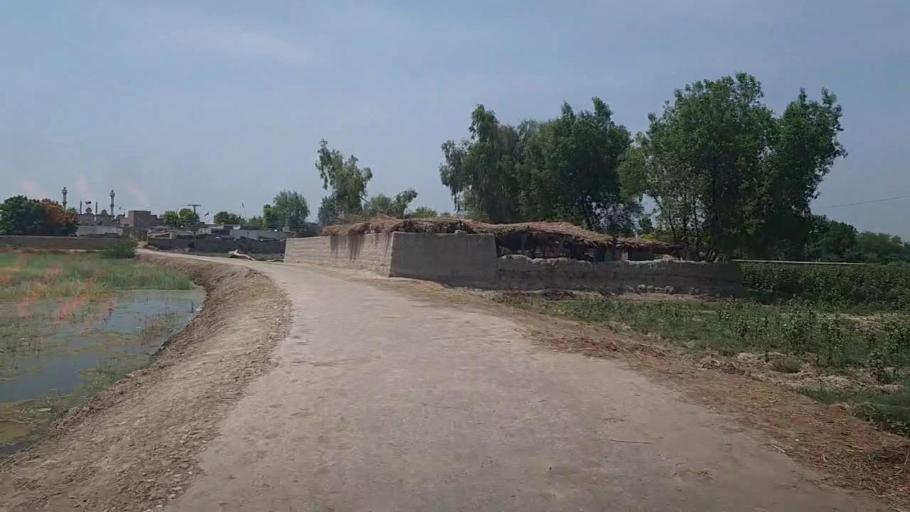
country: PK
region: Sindh
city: Ubauro
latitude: 28.1923
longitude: 69.7710
